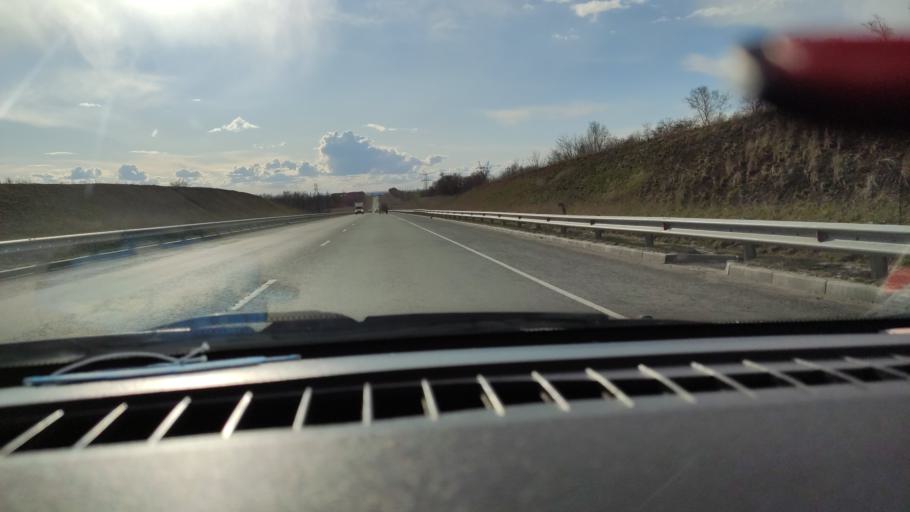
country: RU
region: Saratov
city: Yelshanka
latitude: 51.8223
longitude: 46.3254
